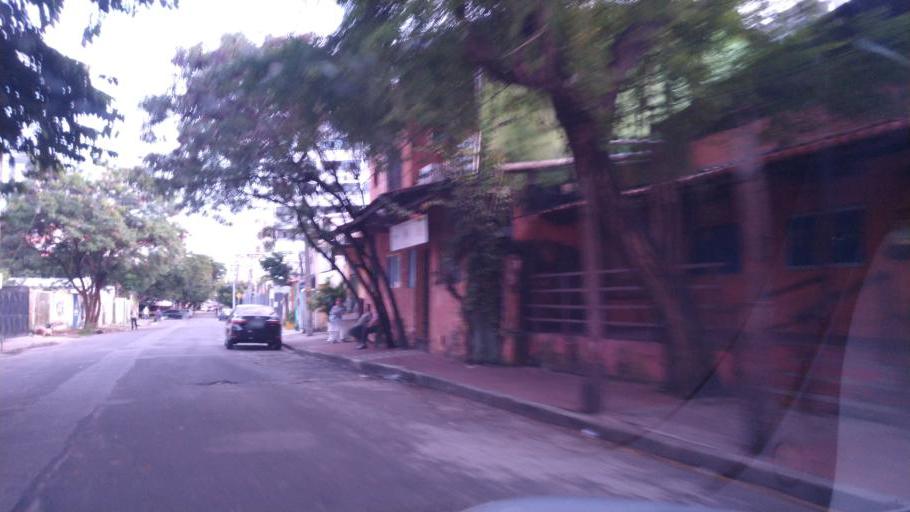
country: BR
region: Ceara
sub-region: Fortaleza
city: Fortaleza
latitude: -3.7305
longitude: -38.4883
